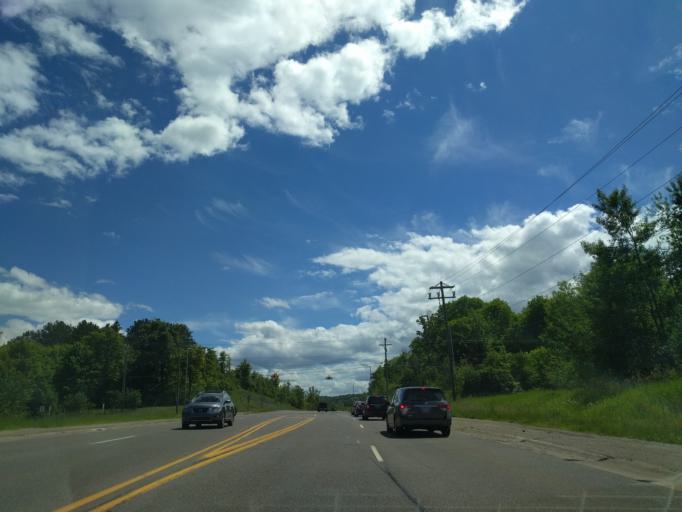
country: US
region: Michigan
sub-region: Marquette County
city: Marquette
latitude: 46.5374
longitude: -87.4171
